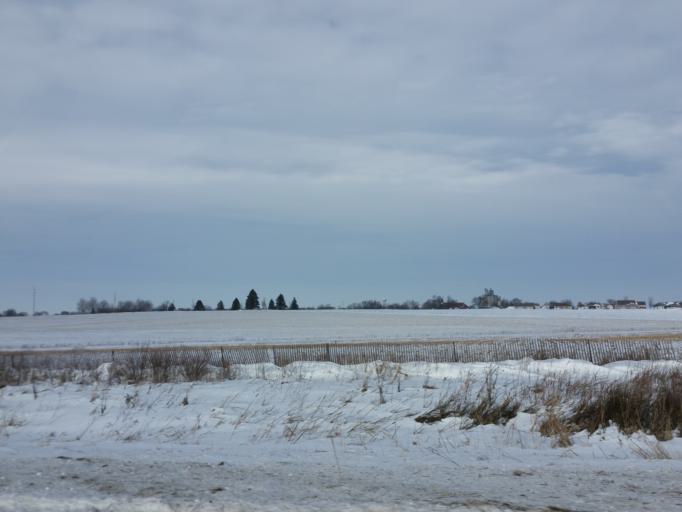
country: US
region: Iowa
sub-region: Buchanan County
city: Independence
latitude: 42.4615
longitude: -91.7304
